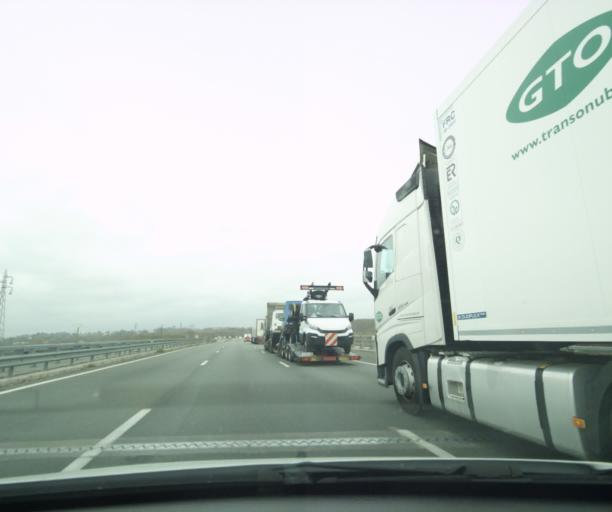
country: FR
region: Aquitaine
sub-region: Departement des Pyrenees-Atlantiques
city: Bayonne
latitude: 43.4653
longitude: -1.4835
